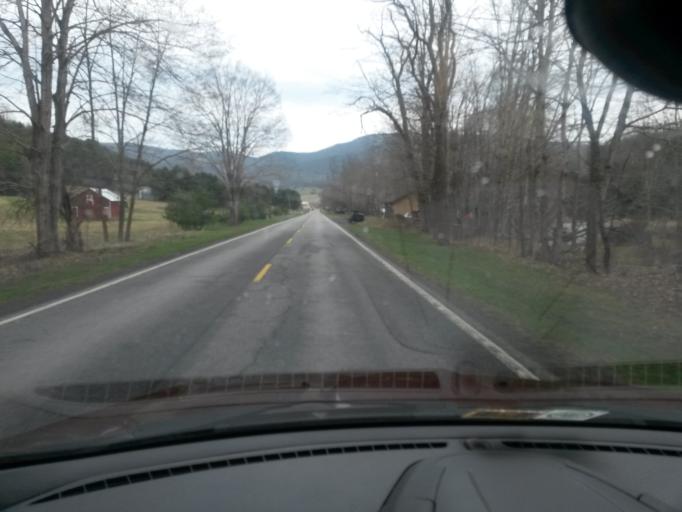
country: US
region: Virginia
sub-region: Highland County
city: Monterey
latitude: 38.3719
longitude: -79.6305
